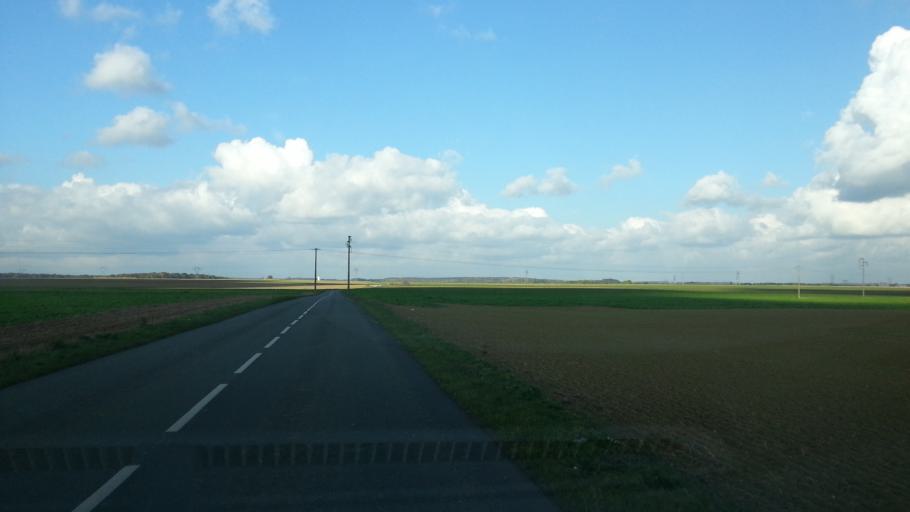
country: FR
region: Picardie
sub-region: Departement de l'Oise
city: Villers-sous-Saint-Leu
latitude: 49.2317
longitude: 2.4120
